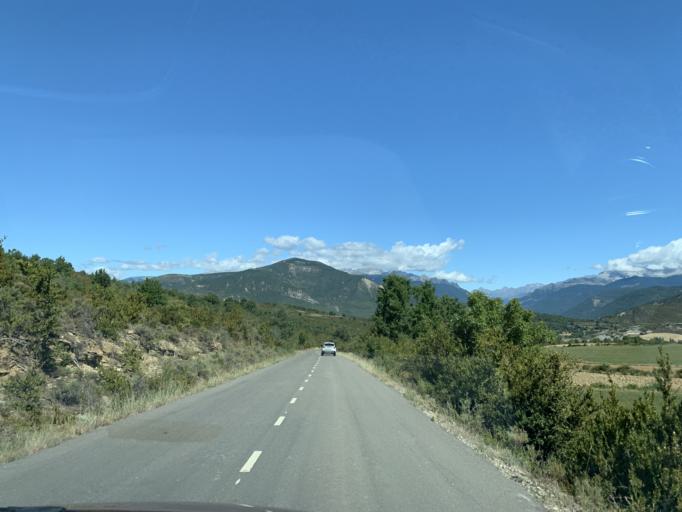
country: ES
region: Aragon
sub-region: Provincia de Huesca
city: Sabinanigo
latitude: 42.5218
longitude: -0.3229
